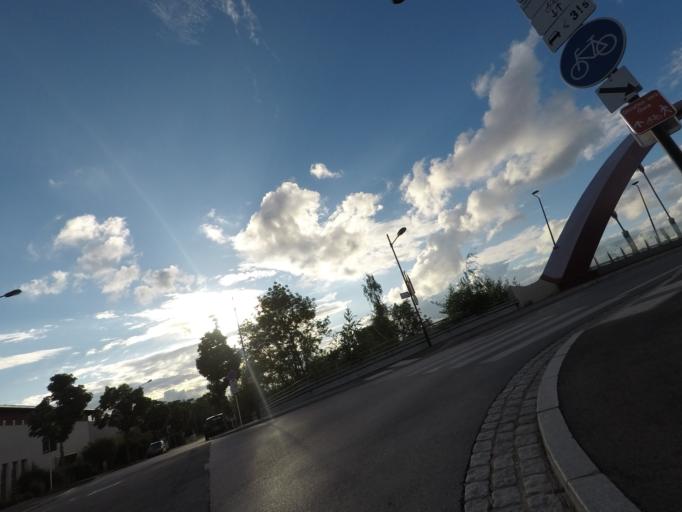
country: LU
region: Luxembourg
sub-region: Canton de Luxembourg
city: Luxembourg
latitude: 49.5940
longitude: 6.1271
